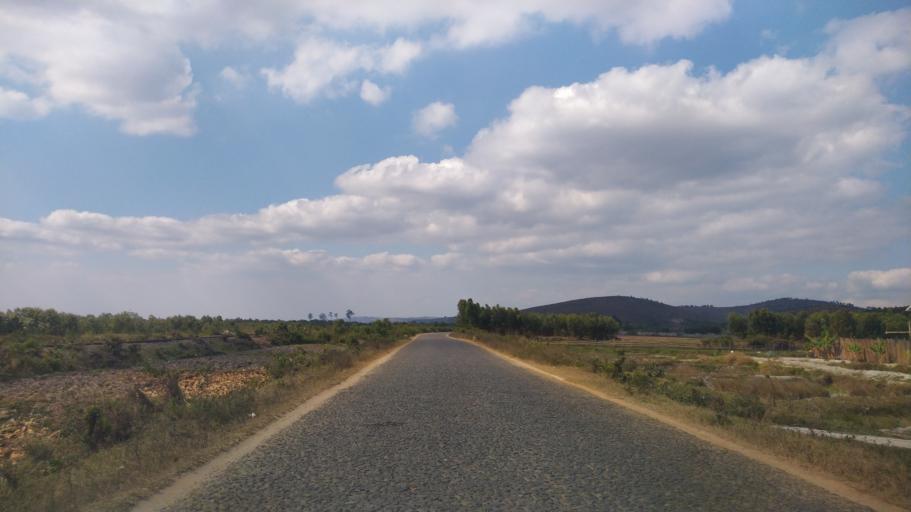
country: MG
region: Alaotra Mangoro
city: Moramanga
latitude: -18.7643
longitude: 48.2548
